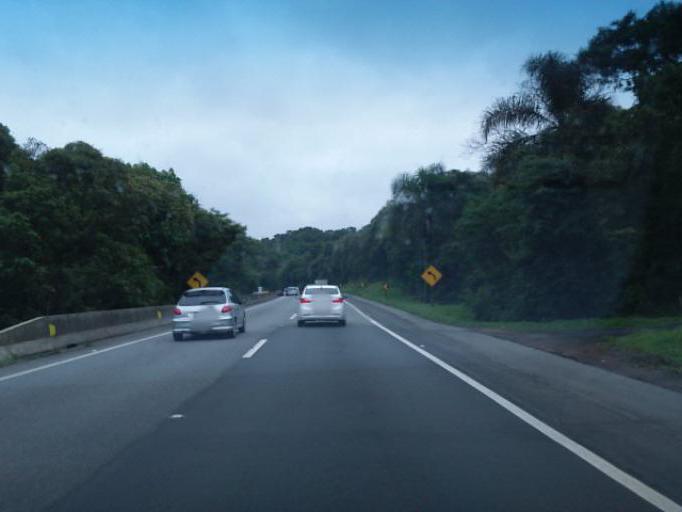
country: BR
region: Parana
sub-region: Sao Jose Dos Pinhais
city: Sao Jose dos Pinhais
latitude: -25.8451
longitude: -49.0136
